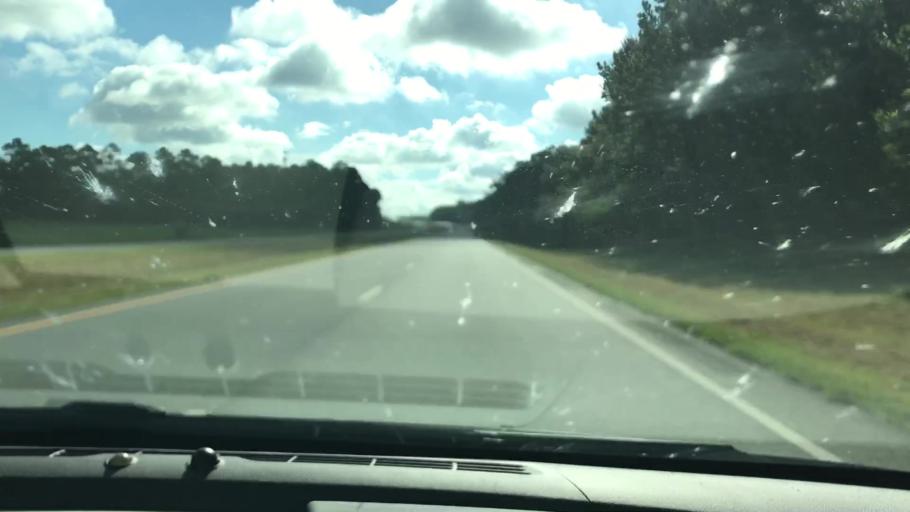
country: US
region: Georgia
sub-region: Worth County
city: Sylvester
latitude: 31.5520
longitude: -83.9455
